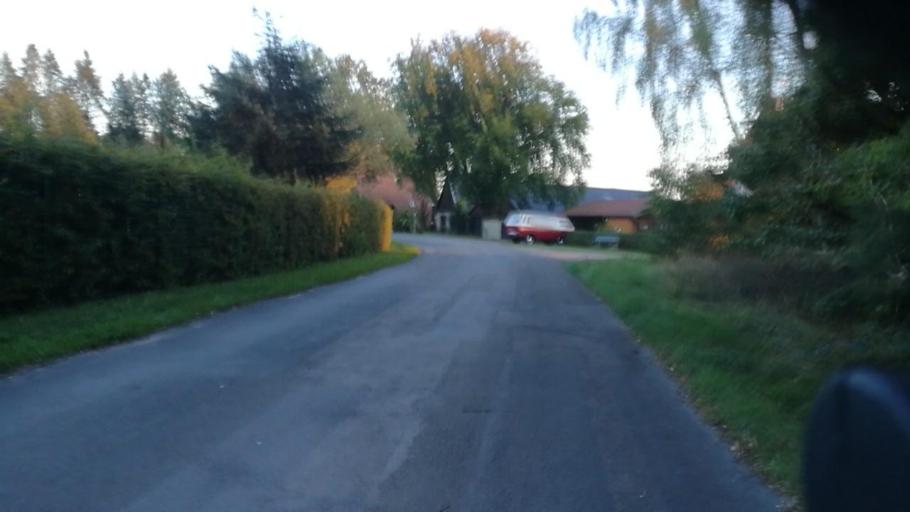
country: DE
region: North Rhine-Westphalia
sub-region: Regierungsbezirk Detmold
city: Steinhagen
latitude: 52.0313
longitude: 8.3886
